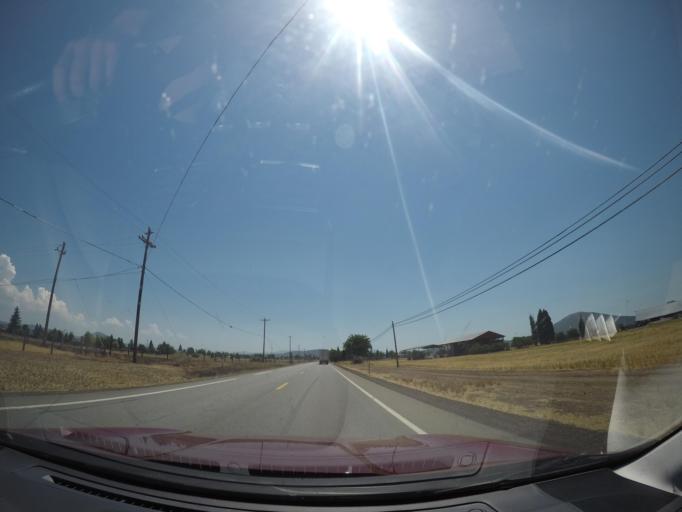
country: US
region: California
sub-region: Shasta County
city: Burney
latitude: 41.0352
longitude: -121.4158
